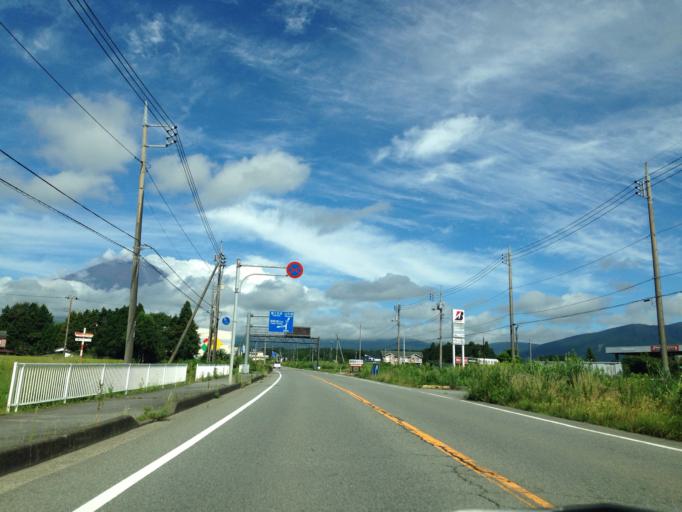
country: JP
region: Shizuoka
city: Gotemba
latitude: 35.3176
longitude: 138.9183
